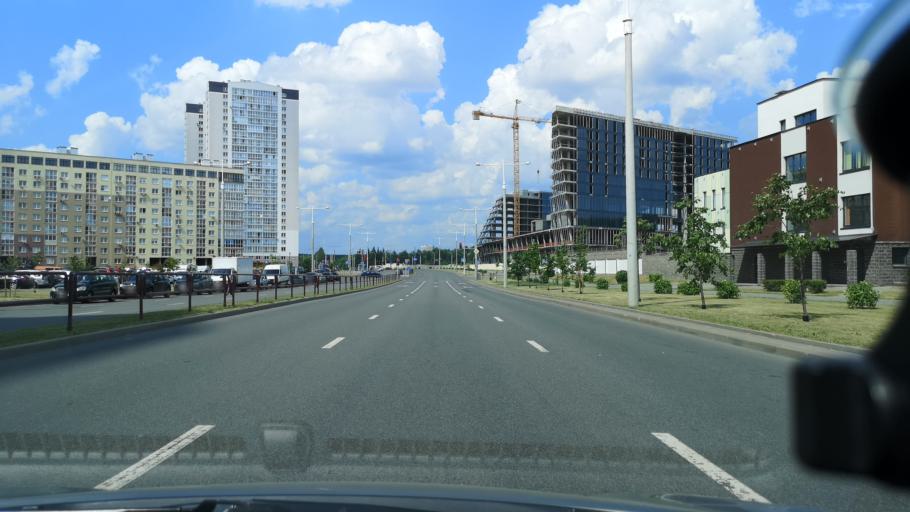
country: BY
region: Minsk
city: Borovlyany
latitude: 53.9315
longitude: 27.6562
